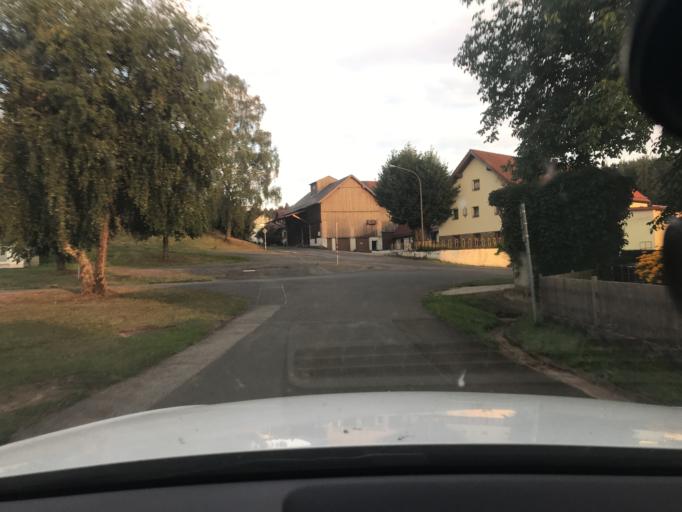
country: DE
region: Bavaria
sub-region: Upper Palatinate
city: Auerbach
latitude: 49.7478
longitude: 11.6196
